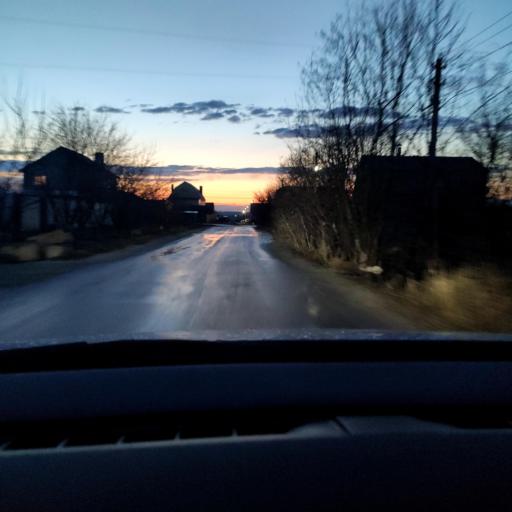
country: RU
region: Voronezj
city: Semiluki
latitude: 51.7123
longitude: 39.0220
